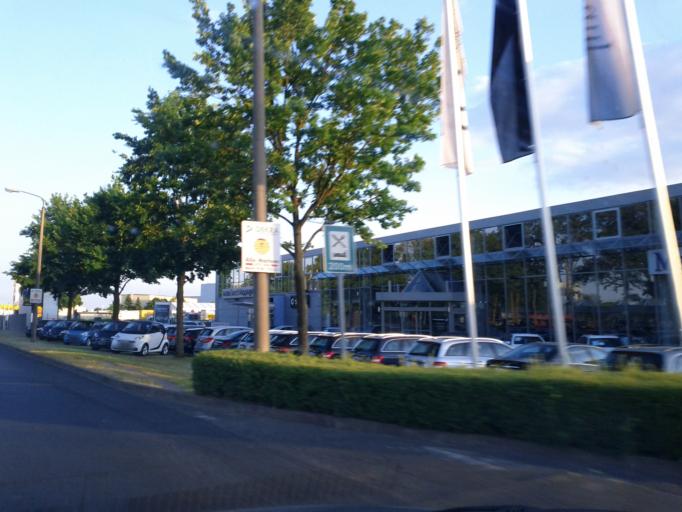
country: DE
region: Brandenburg
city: Hoppegarten
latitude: 52.5144
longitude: 13.6502
